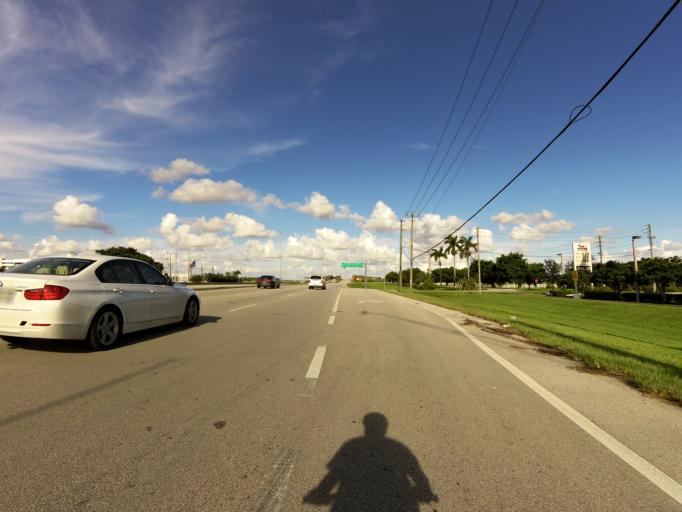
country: US
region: Florida
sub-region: Broward County
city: Southwest Ranches
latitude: 26.0624
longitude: -80.3620
